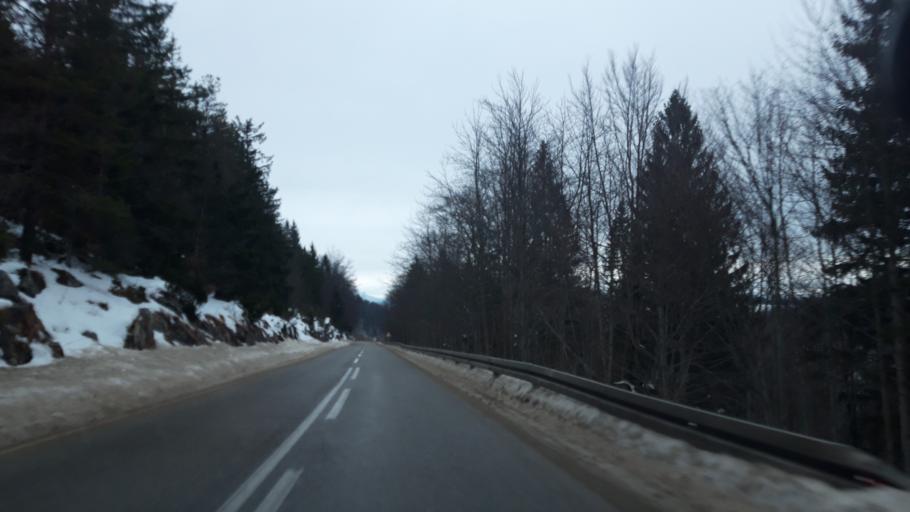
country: BA
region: Republika Srpska
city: Vlasenica
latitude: 44.1404
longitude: 18.9499
